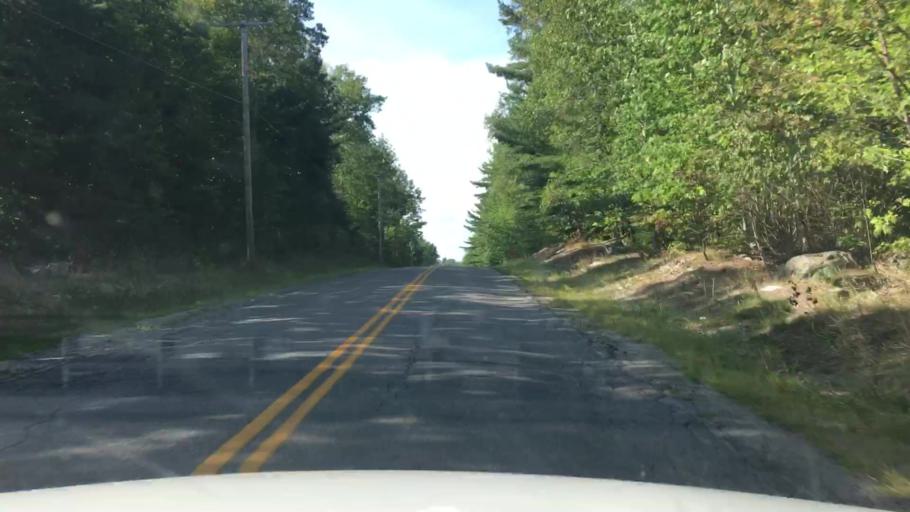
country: US
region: Maine
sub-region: Penobscot County
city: Enfield
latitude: 45.2103
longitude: -68.5232
